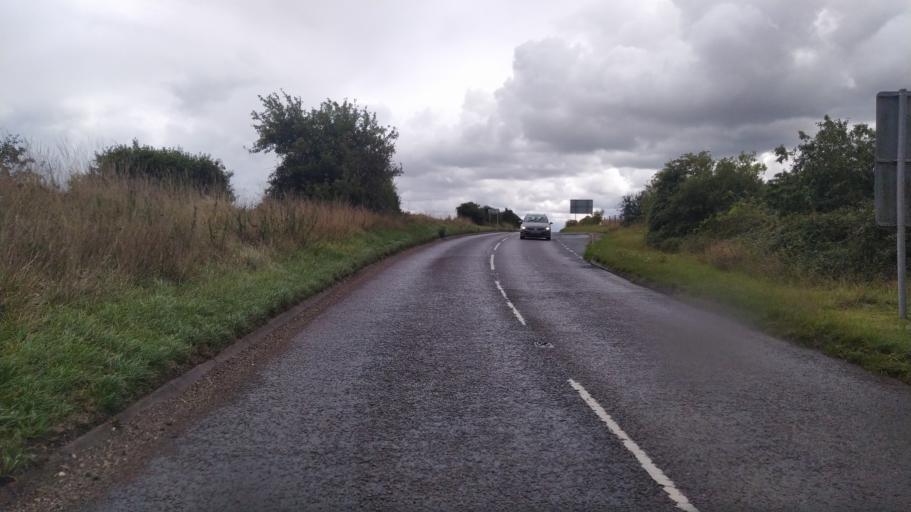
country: GB
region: England
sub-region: Wiltshire
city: Bower Chalke
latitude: 50.9487
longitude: -1.9842
